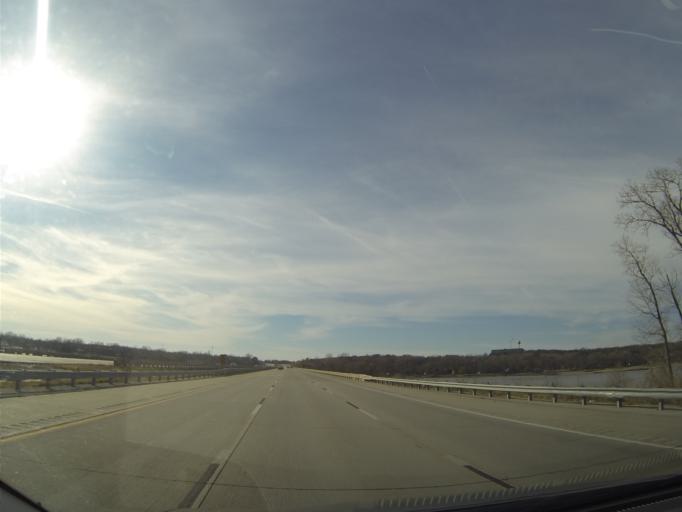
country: US
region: Nebraska
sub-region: Saunders County
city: Ashland
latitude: 41.0298
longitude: -96.2945
